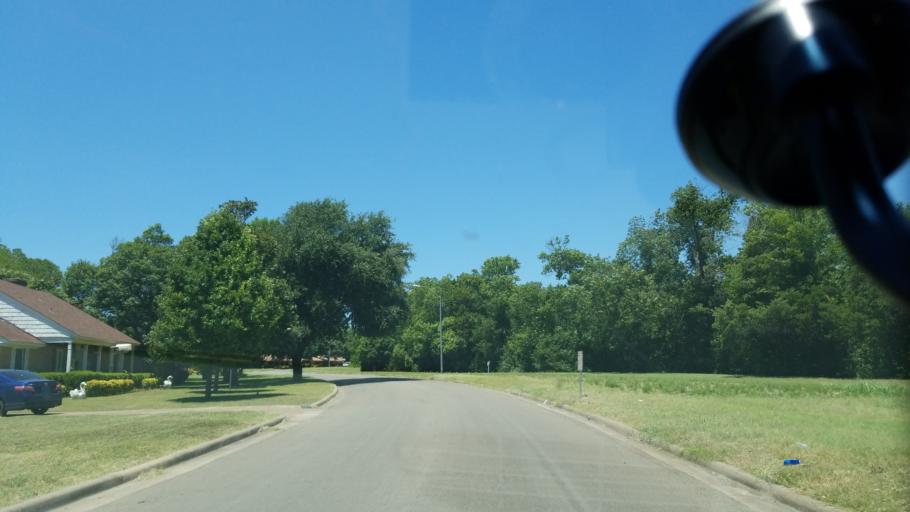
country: US
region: Texas
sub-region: Dallas County
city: Cockrell Hill
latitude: 32.6938
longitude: -96.8343
